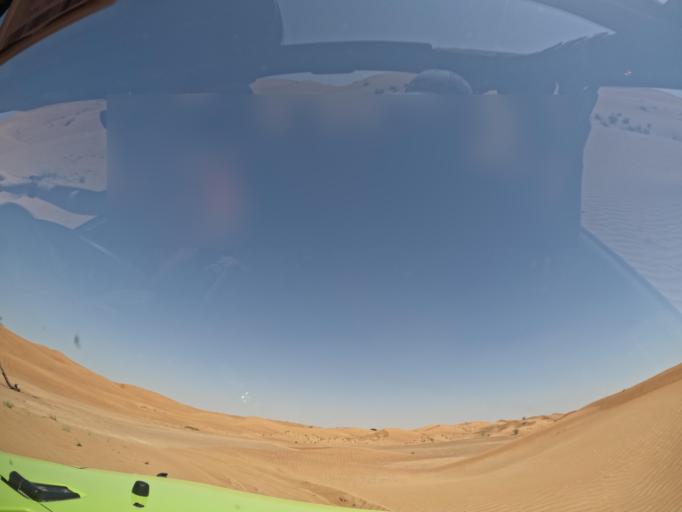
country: AE
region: Ash Shariqah
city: Adh Dhayd
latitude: 24.9877
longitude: 55.7243
